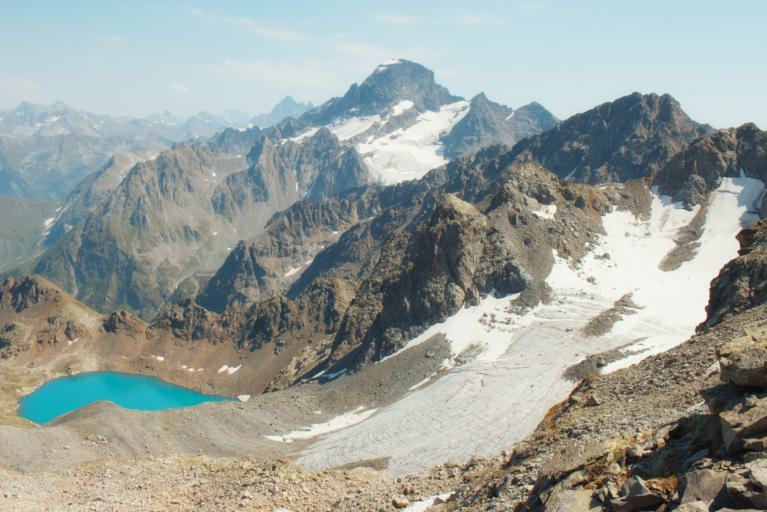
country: RU
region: Karachayevo-Cherkesiya
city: Nizhniy Arkhyz
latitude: 43.4535
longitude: 41.2177
